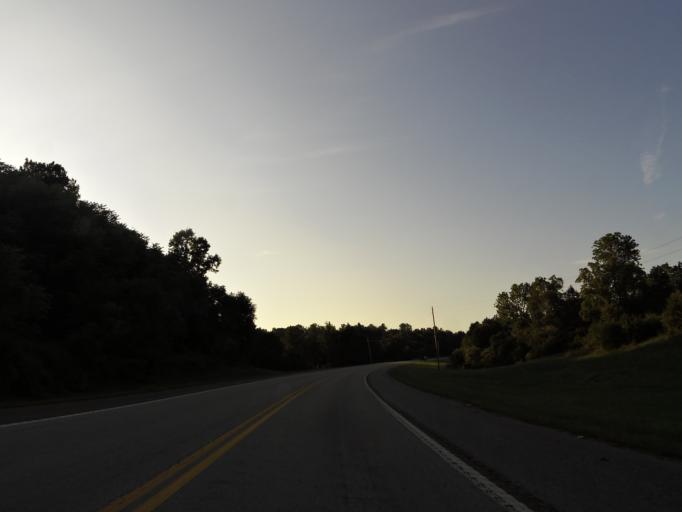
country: US
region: Tennessee
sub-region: Meigs County
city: Decatur
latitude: 35.5749
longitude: -84.6756
